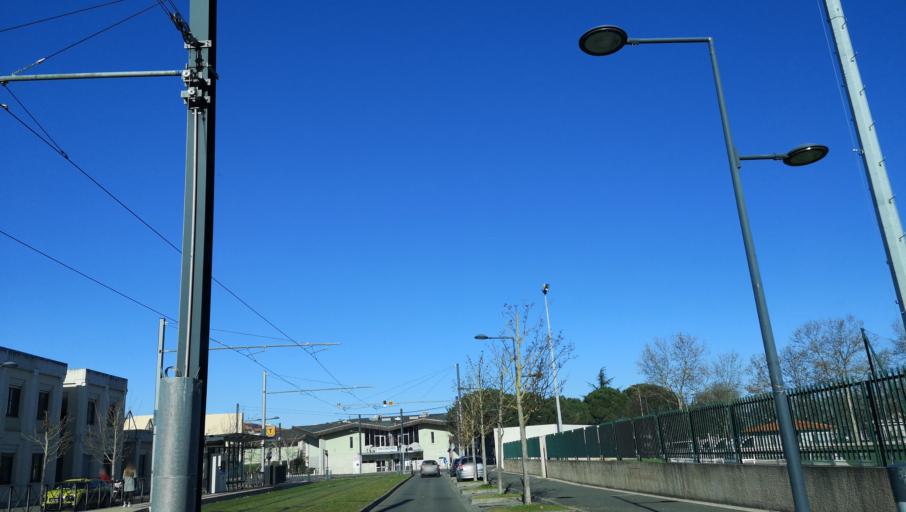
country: FR
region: Midi-Pyrenees
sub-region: Departement de la Haute-Garonne
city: Blagnac
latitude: 43.6397
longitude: 1.3830
